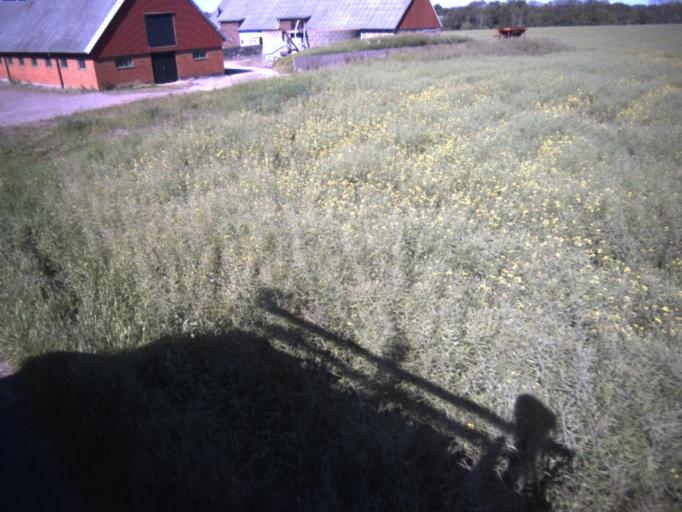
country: SE
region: Skane
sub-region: Helsingborg
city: Gantofta
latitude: 55.9816
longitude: 12.8124
